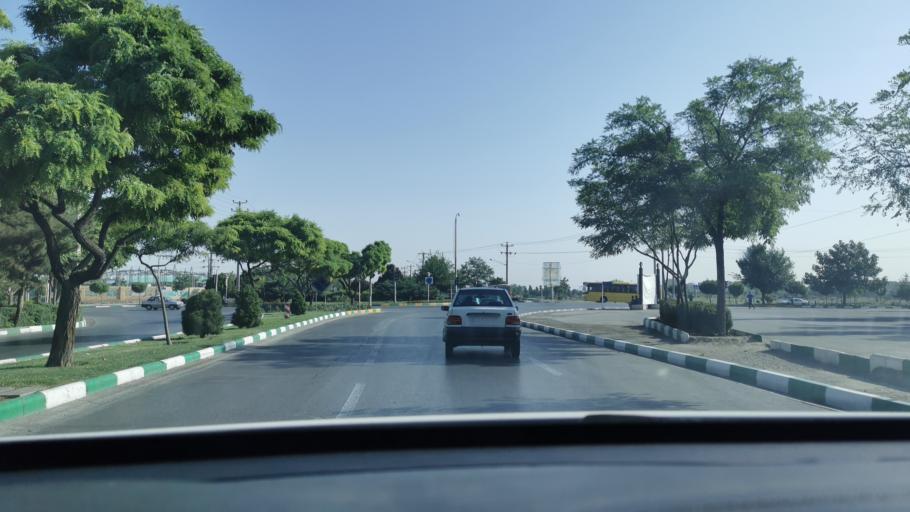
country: IR
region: Razavi Khorasan
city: Mashhad
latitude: 36.3403
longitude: 59.5077
